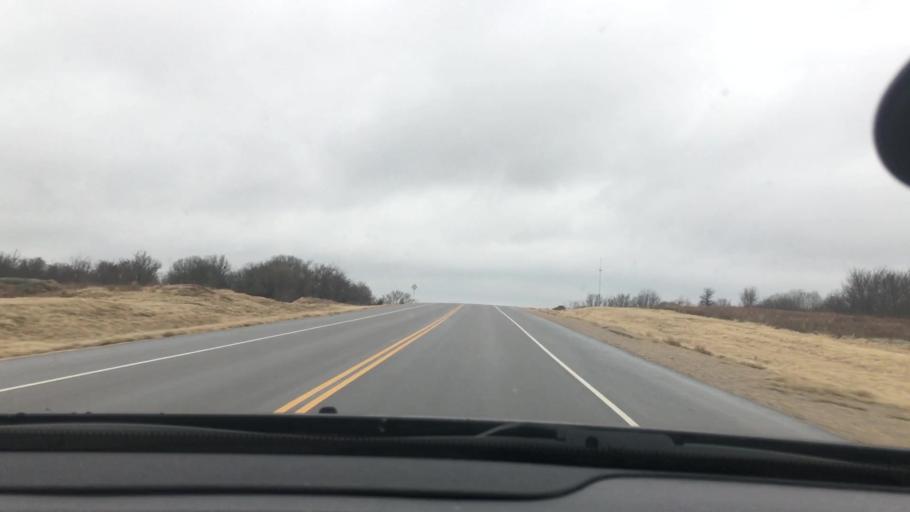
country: US
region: Oklahoma
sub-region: Johnston County
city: Tishomingo
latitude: 34.3283
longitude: -96.6592
